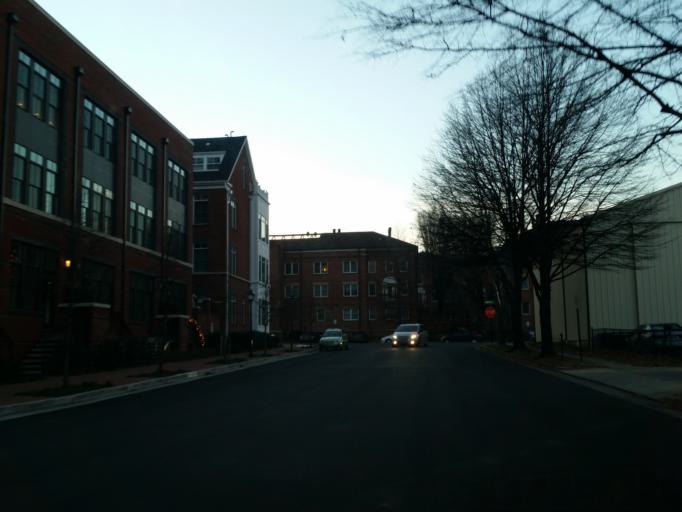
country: US
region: Virginia
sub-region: City of Alexandria
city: Alexandria
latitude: 38.8170
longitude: -77.0401
